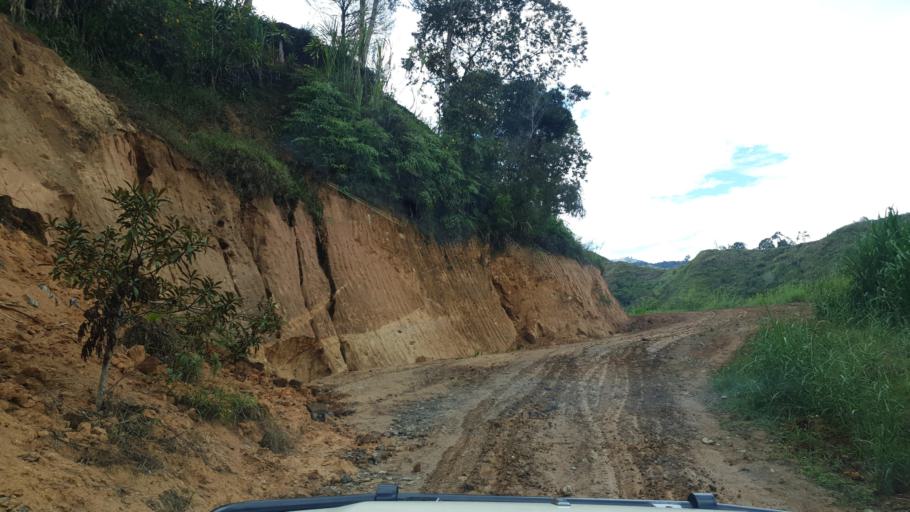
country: PG
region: Eastern Highlands
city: Goroka
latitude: -5.9236
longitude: 145.2634
